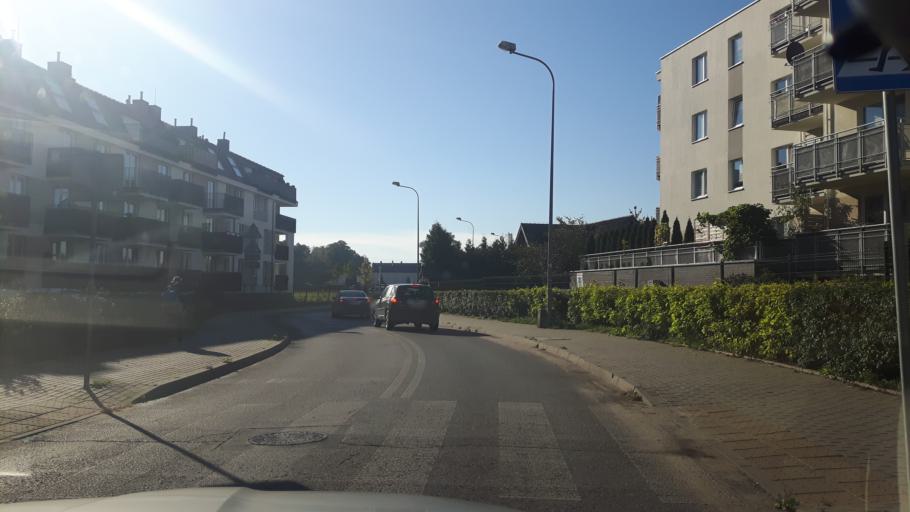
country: PL
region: Masovian Voivodeship
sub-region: Powiat legionowski
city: Stanislawow Pierwszy
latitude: 52.3611
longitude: 21.0391
